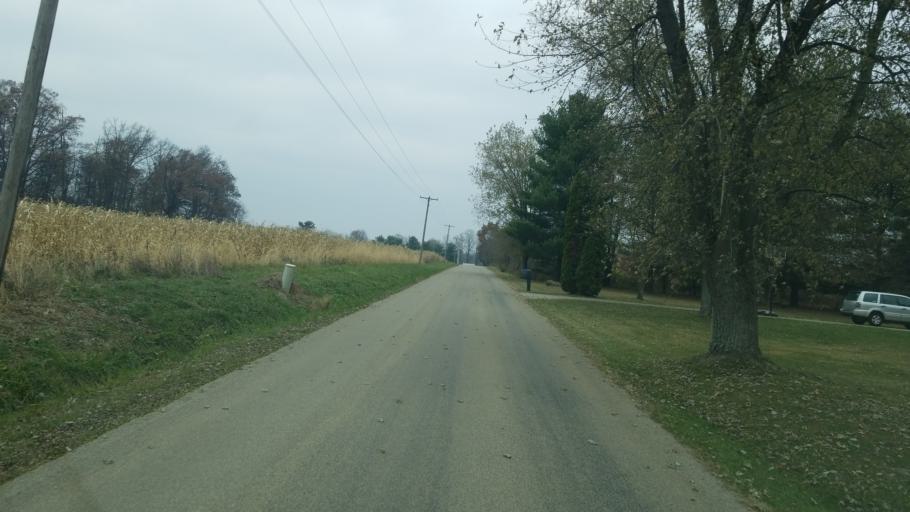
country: US
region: Ohio
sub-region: Knox County
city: Gambier
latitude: 40.3502
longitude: -82.4280
